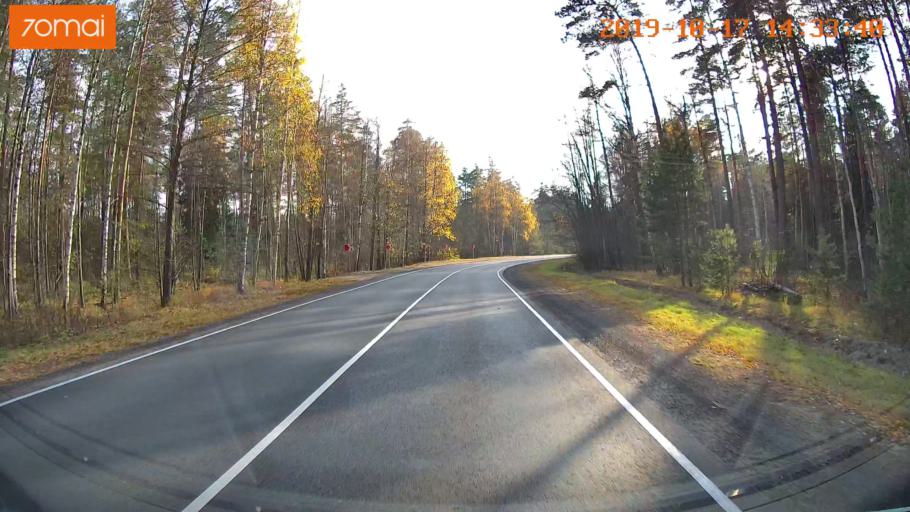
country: RU
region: Rjazan
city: Solotcha
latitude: 54.9211
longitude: 39.9977
